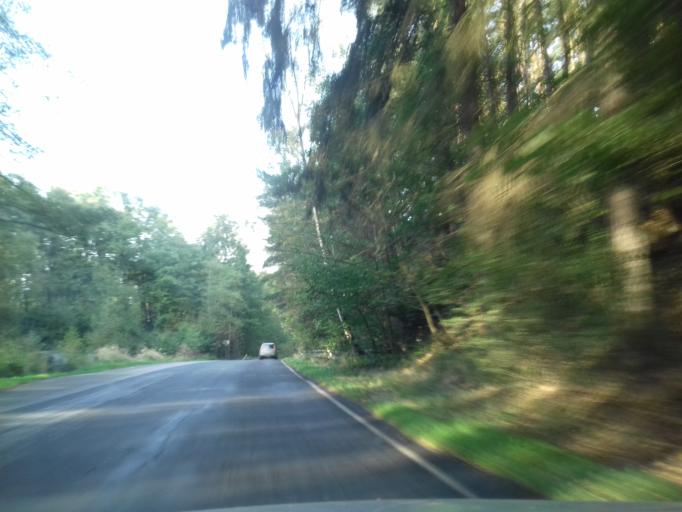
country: CZ
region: Central Bohemia
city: Kamenny Privoz
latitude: 49.8549
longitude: 14.5040
